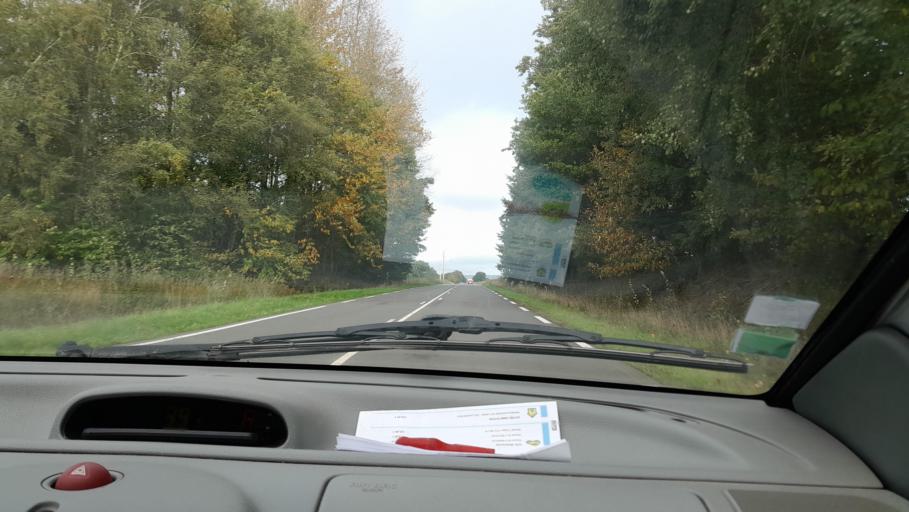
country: FR
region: Brittany
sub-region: Departement d'Ille-et-Vilaine
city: Beauce
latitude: 48.2973
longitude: -1.1624
